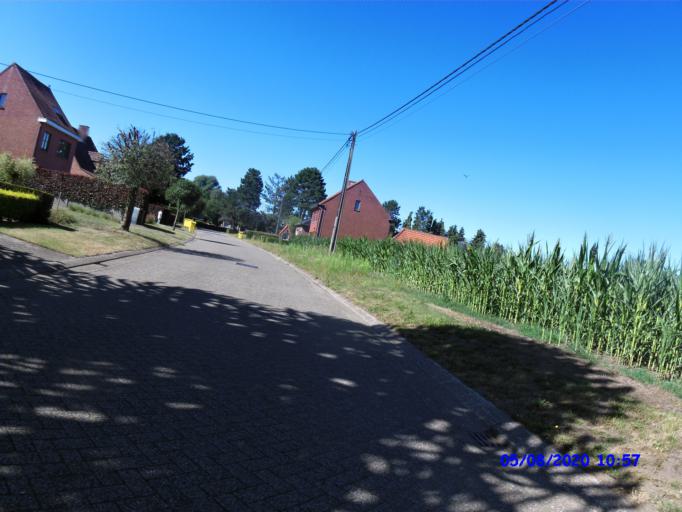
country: BE
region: Flanders
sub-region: Provincie Antwerpen
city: Lille
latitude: 51.2403
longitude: 4.8884
